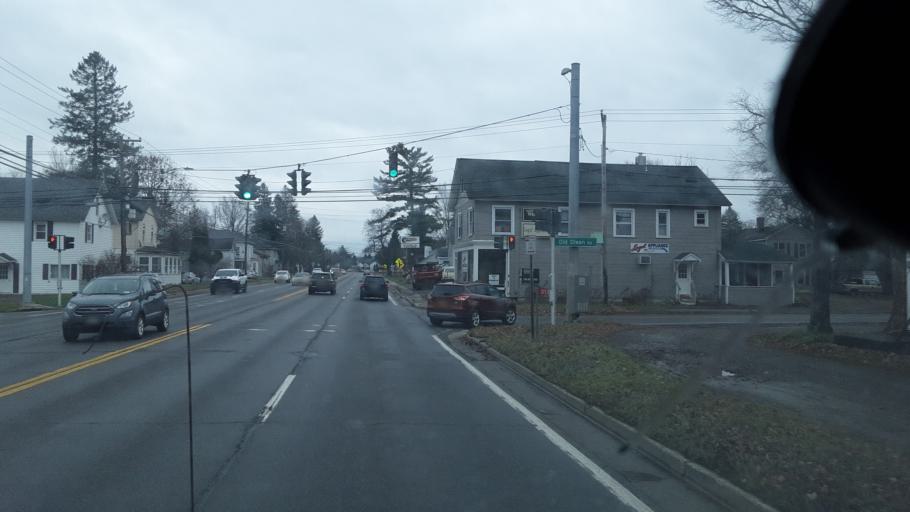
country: US
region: New York
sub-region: Cattaraugus County
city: Yorkshire
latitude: 42.5301
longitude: -78.4731
